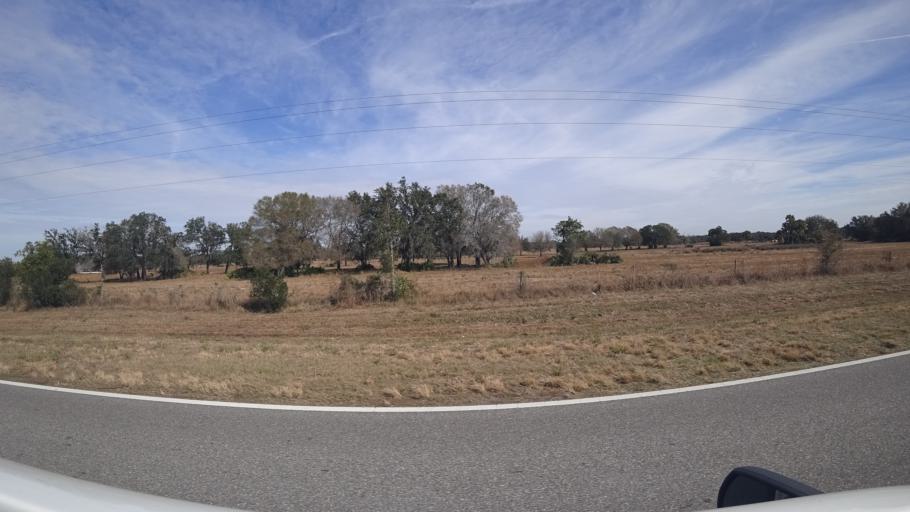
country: US
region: Florida
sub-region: Hillsborough County
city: Sun City Center
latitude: 27.5635
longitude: -82.3753
